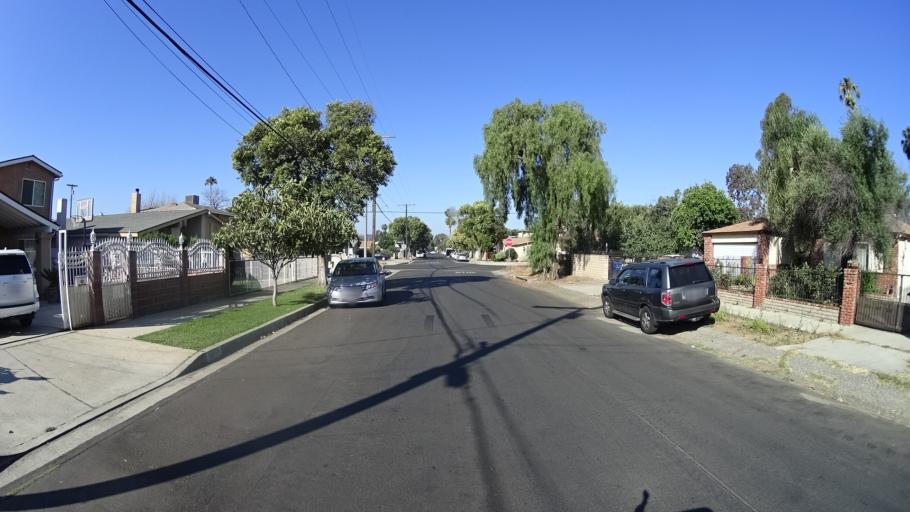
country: US
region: California
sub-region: Los Angeles County
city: Van Nuys
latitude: 34.2247
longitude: -118.4245
